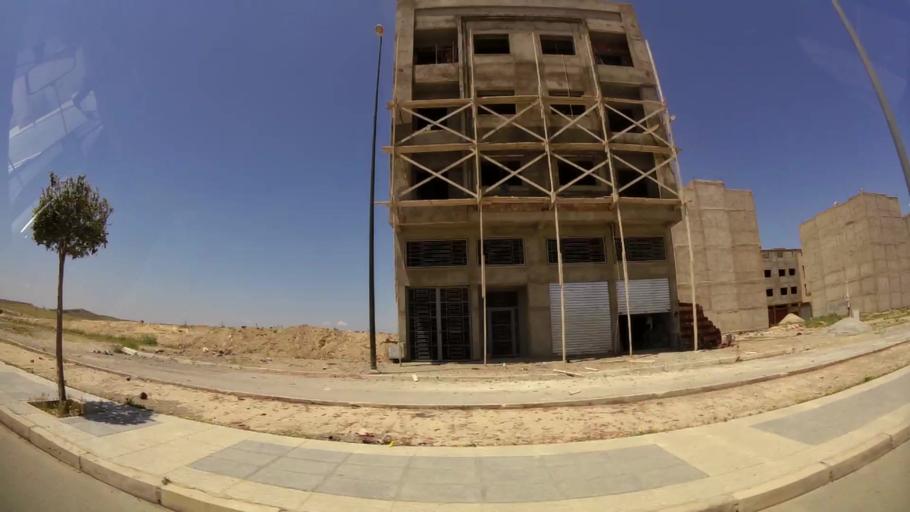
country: MA
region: Oriental
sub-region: Oujda-Angad
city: Oujda
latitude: 34.6576
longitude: -1.9541
